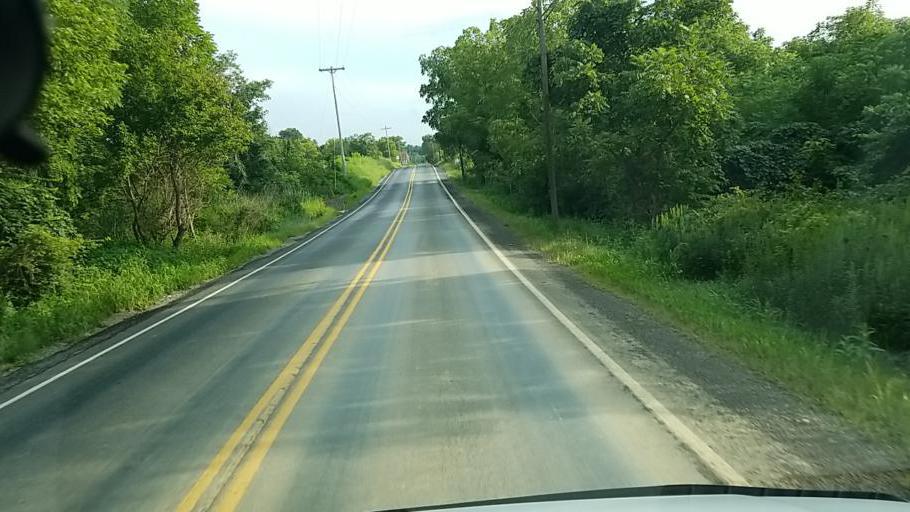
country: US
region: Pennsylvania
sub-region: Cumberland County
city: Newville
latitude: 40.2486
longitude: -77.4438
